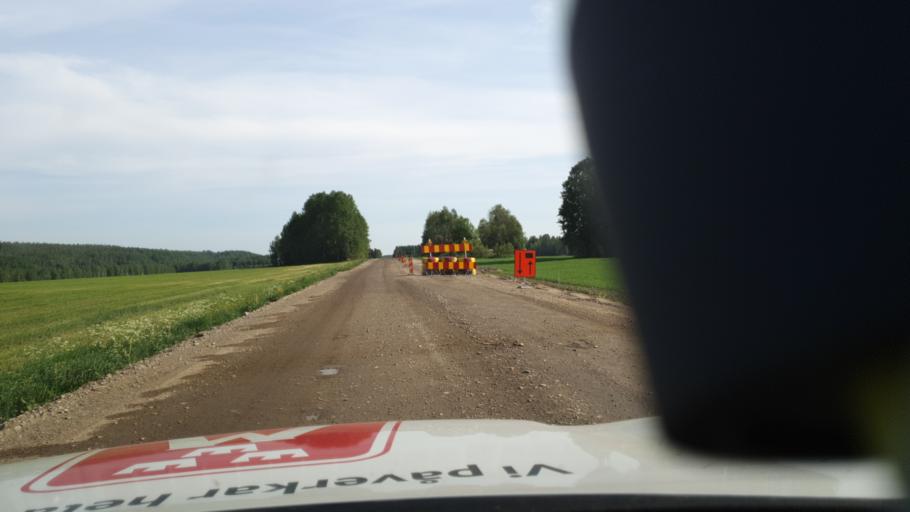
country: SE
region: Vaesterbotten
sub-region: Robertsfors Kommun
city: Robertsfors
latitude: 64.3164
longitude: 21.0242
